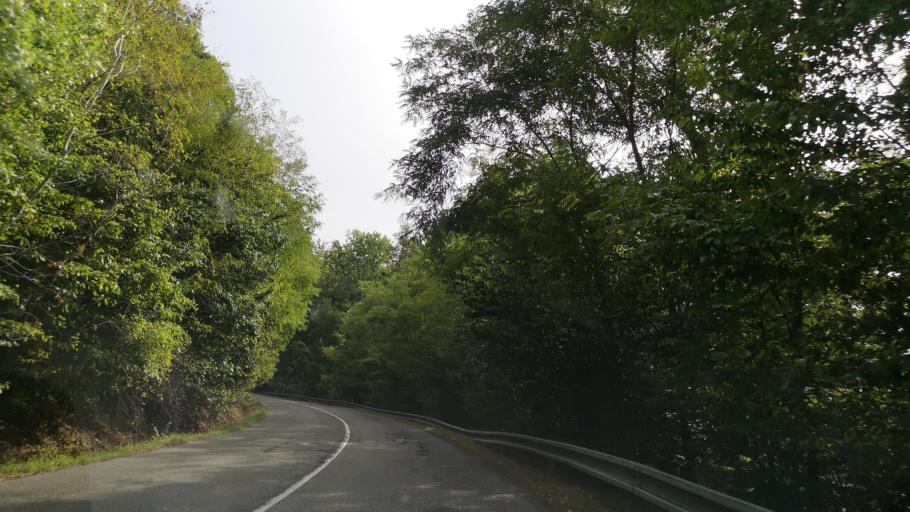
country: SK
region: Banskobystricky
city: Revuca
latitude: 48.5855
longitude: 20.0596
